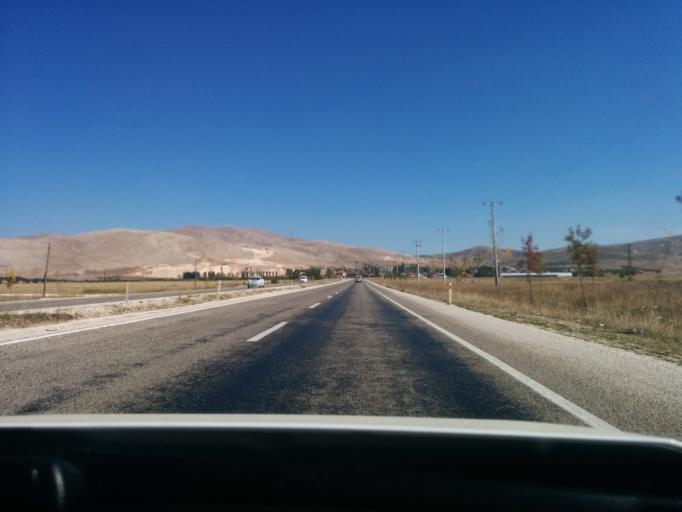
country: TR
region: Antalya
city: Kizilcadag
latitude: 37.0082
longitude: 29.9413
